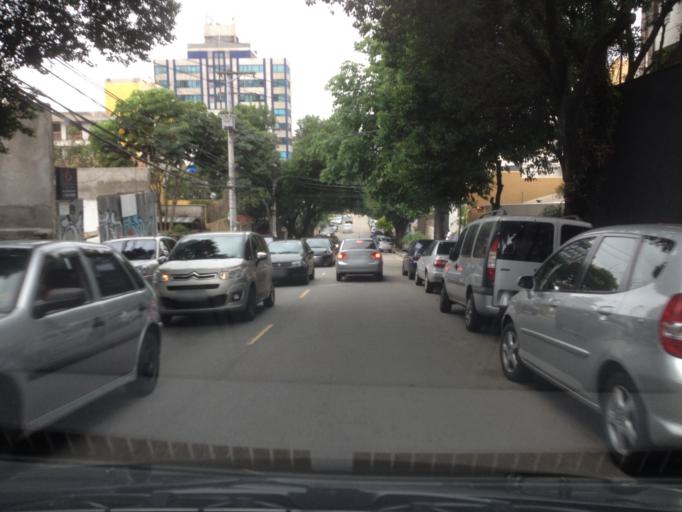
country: BR
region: Sao Paulo
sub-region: Sao Paulo
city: Sao Paulo
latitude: -23.5570
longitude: -46.6881
